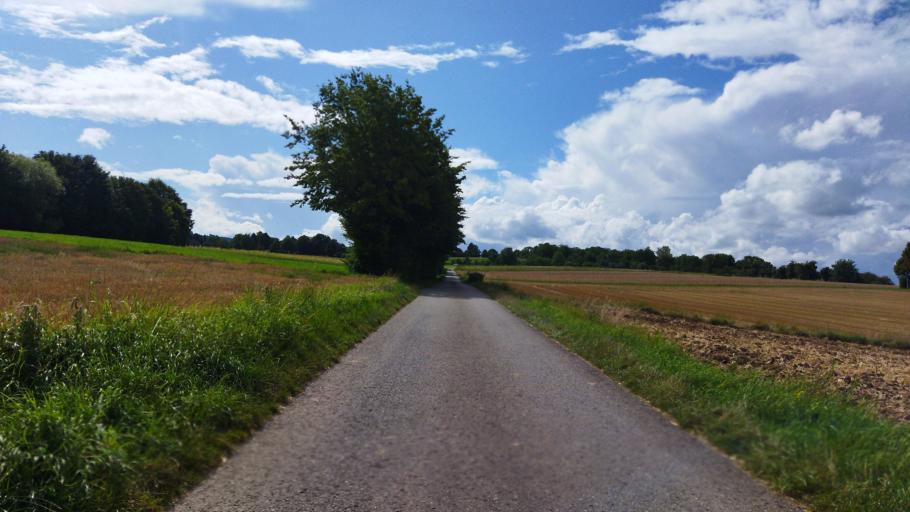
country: DE
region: Baden-Wuerttemberg
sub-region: Regierungsbezirk Stuttgart
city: Bonnigheim
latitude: 49.0314
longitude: 9.0900
